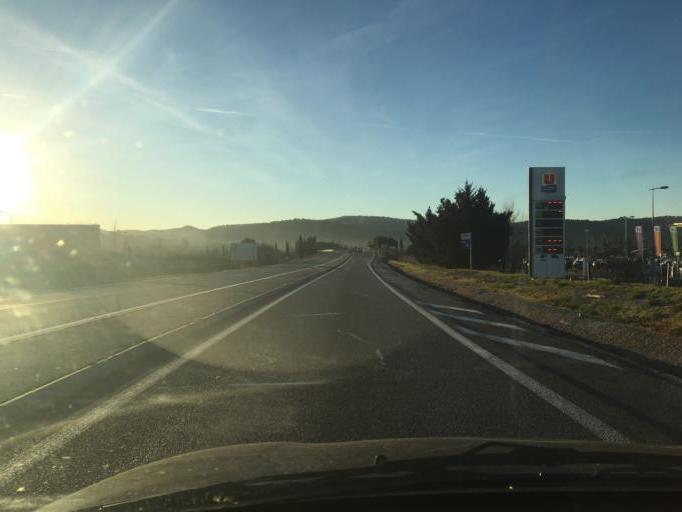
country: FR
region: Provence-Alpes-Cote d'Azur
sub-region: Departement du Var
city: Les Arcs
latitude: 43.4530
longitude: 6.4910
